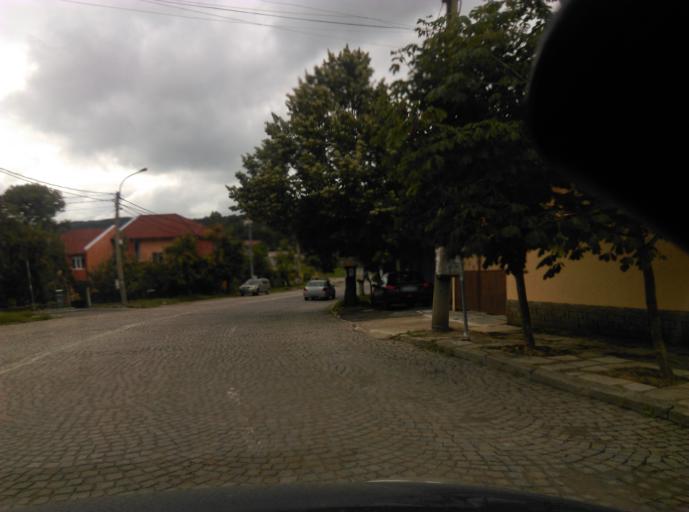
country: BG
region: Sofia-Capital
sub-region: Stolichna Obshtina
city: Sofia
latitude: 42.6112
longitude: 23.3405
